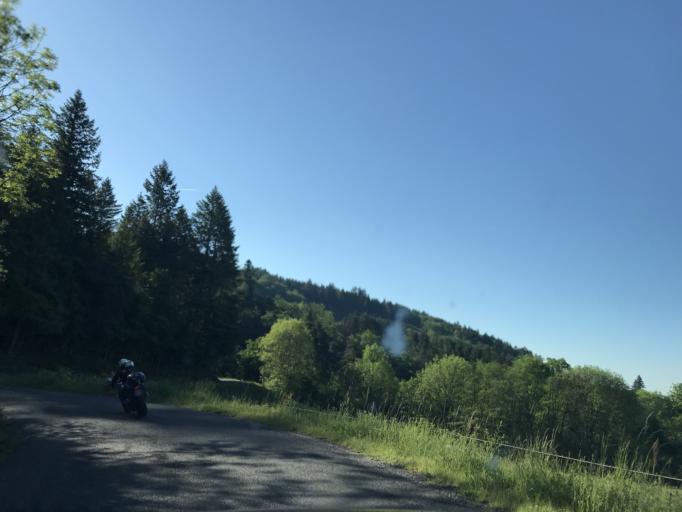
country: FR
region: Auvergne
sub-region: Departement du Puy-de-Dome
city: Job
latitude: 45.6817
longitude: 3.6972
